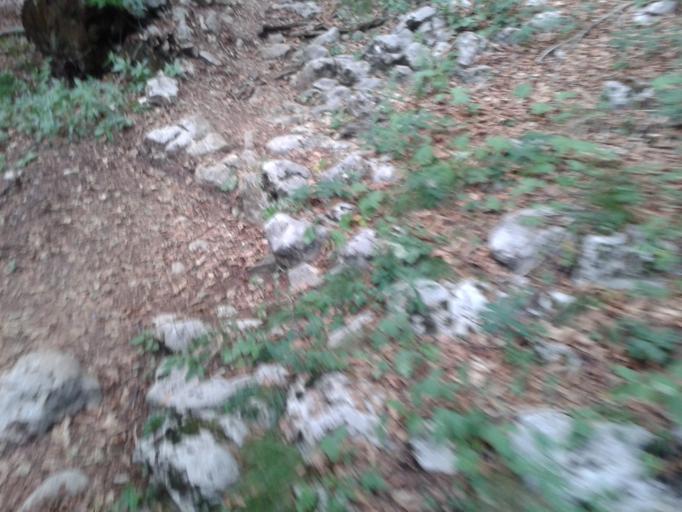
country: IT
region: Trentino-Alto Adige
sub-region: Provincia di Trento
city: Brentonico
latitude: 45.7844
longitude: 10.9062
